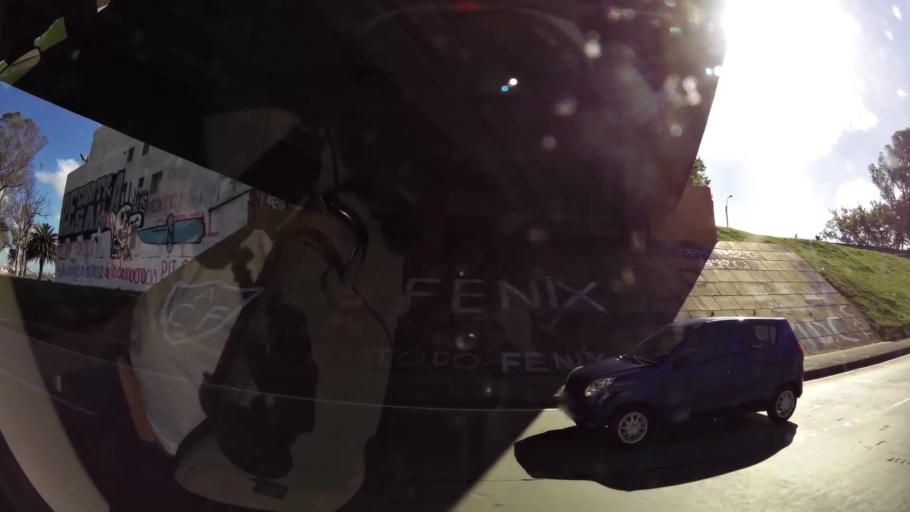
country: UY
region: Montevideo
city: Montevideo
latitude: -34.8727
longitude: -56.2163
